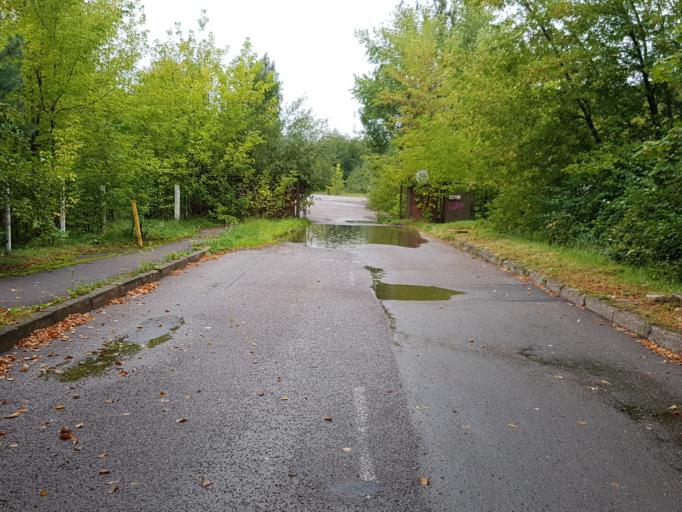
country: LT
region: Vilnius County
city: Lazdynai
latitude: 54.6554
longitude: 25.1940
